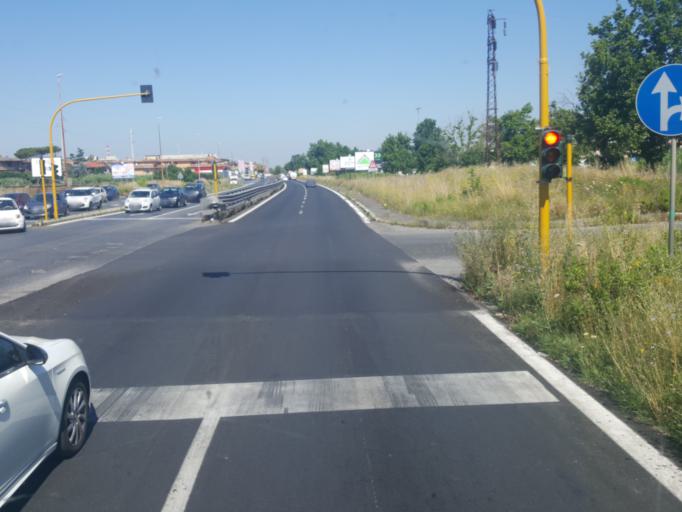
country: IT
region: Latium
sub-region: Citta metropolitana di Roma Capitale
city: Ciampino
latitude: 41.8343
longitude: 12.6069
